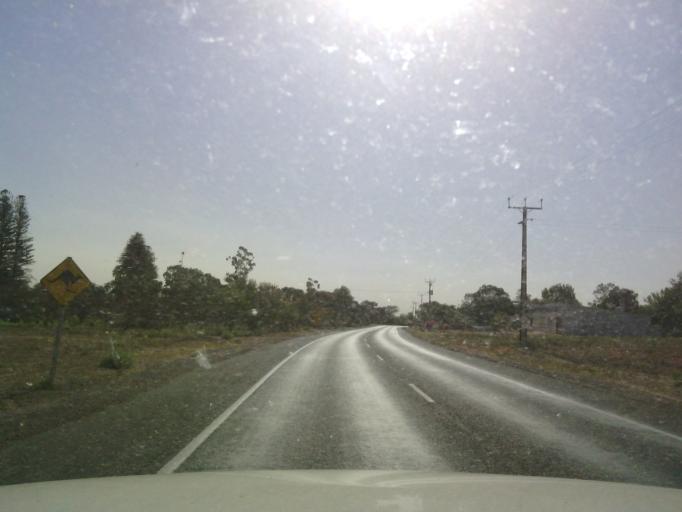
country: AU
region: South Australia
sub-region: Berri and Barmera
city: Berri
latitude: -34.2821
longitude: 140.5873
